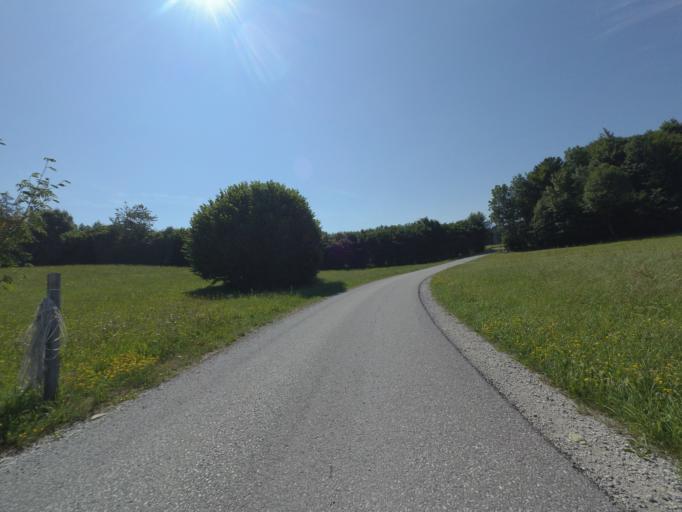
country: AT
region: Salzburg
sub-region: Politischer Bezirk Hallein
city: Adnet
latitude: 47.6835
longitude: 13.1282
